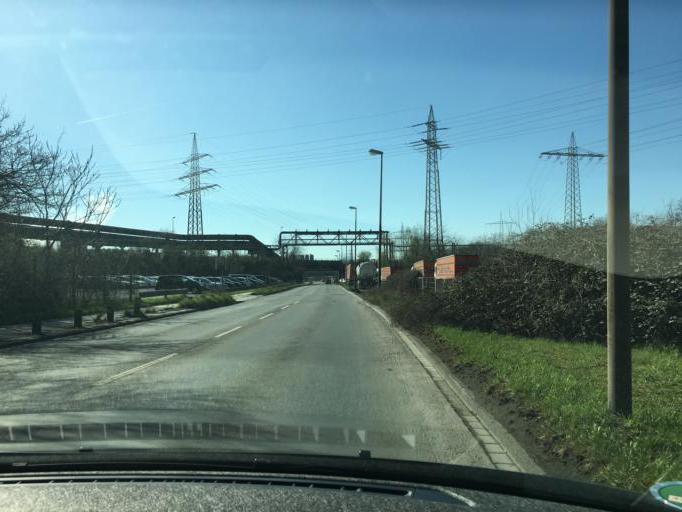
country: DE
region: North Rhine-Westphalia
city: Meiderich
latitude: 51.4892
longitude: 6.7255
